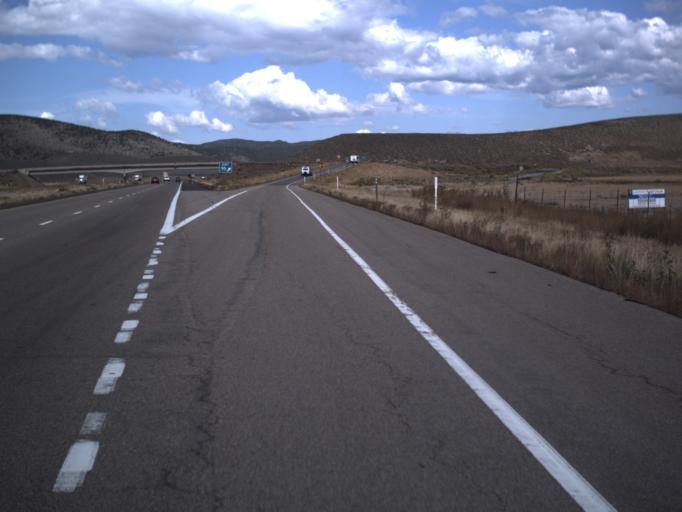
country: US
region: Utah
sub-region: Beaver County
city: Beaver
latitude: 38.0667
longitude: -112.6910
